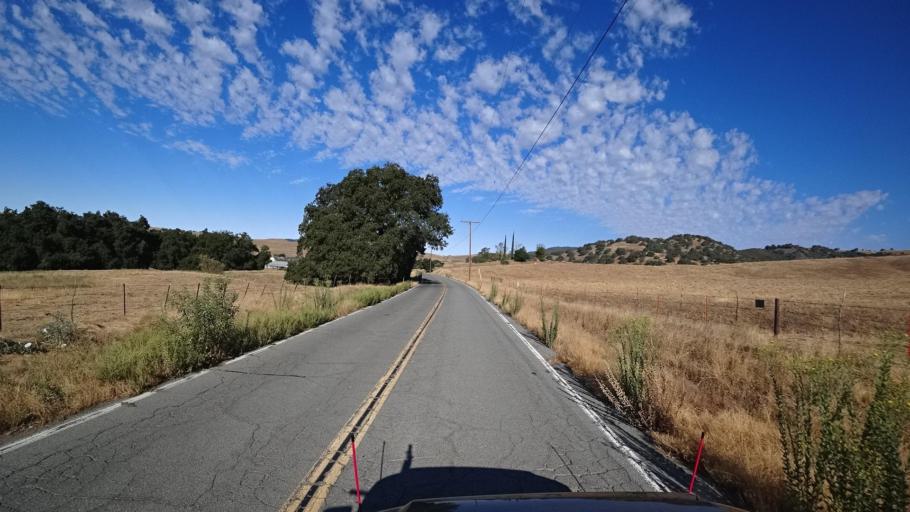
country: US
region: California
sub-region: San Diego County
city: Julian
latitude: 33.1590
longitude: -116.7191
